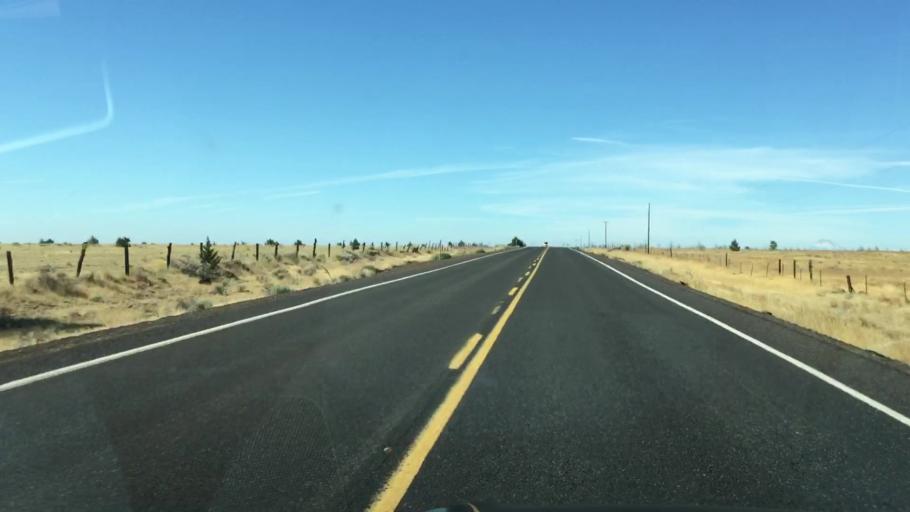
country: US
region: Oregon
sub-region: Jefferson County
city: Madras
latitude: 44.9415
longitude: -120.9226
